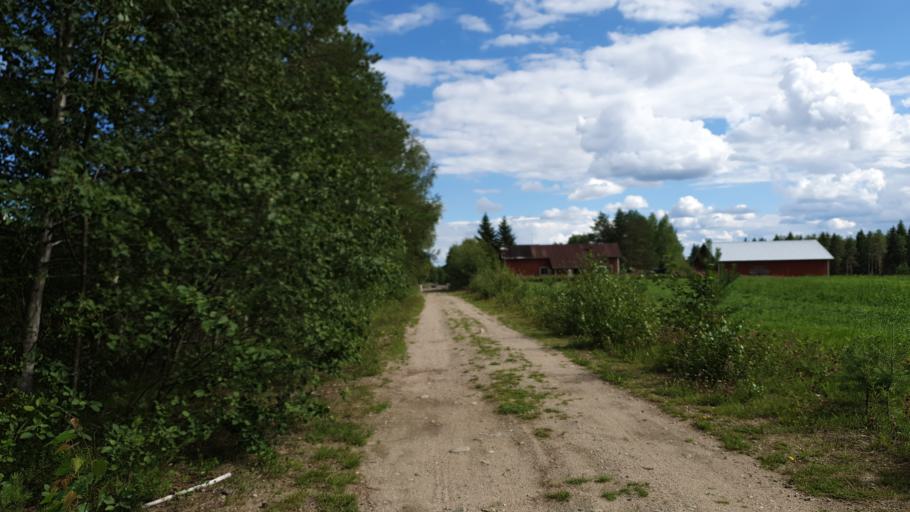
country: FI
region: Kainuu
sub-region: Kehys-Kainuu
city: Kuhmo
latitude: 64.1137
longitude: 29.5215
